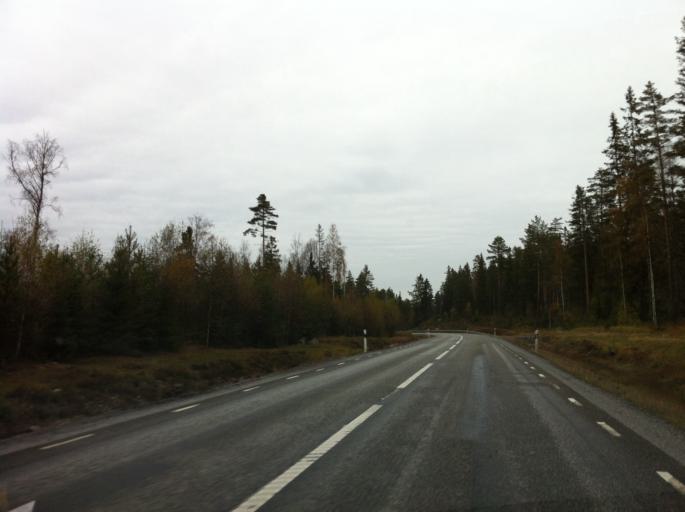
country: SE
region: OErebro
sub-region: Ljusnarsbergs Kommun
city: Kopparberg
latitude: 59.9347
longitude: 15.0241
